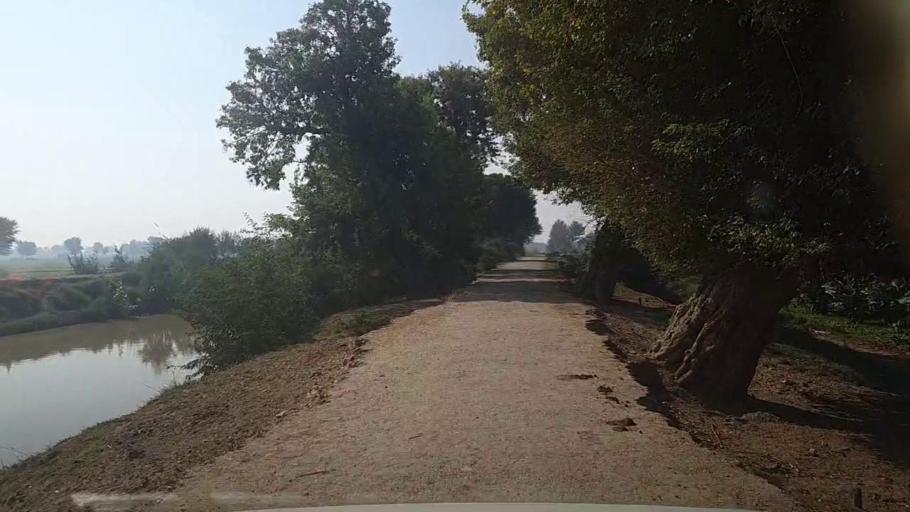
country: PK
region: Sindh
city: Kandiari
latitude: 27.0050
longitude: 68.4941
